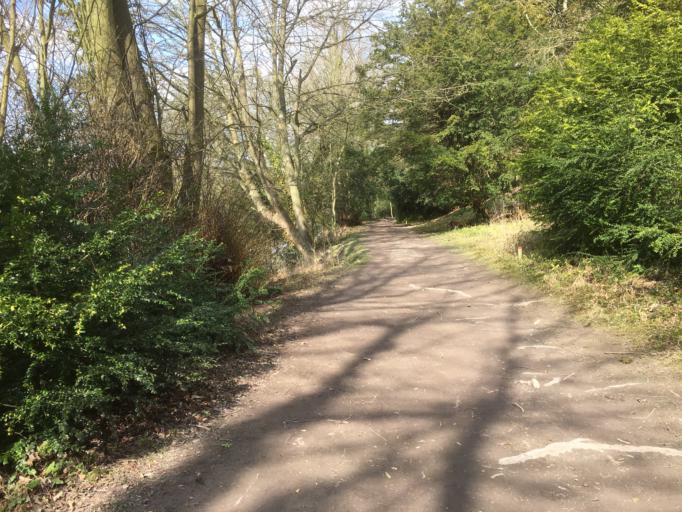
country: GB
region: England
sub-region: Royal Borough of Windsor and Maidenhead
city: Cookham
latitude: 51.5494
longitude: -0.6909
